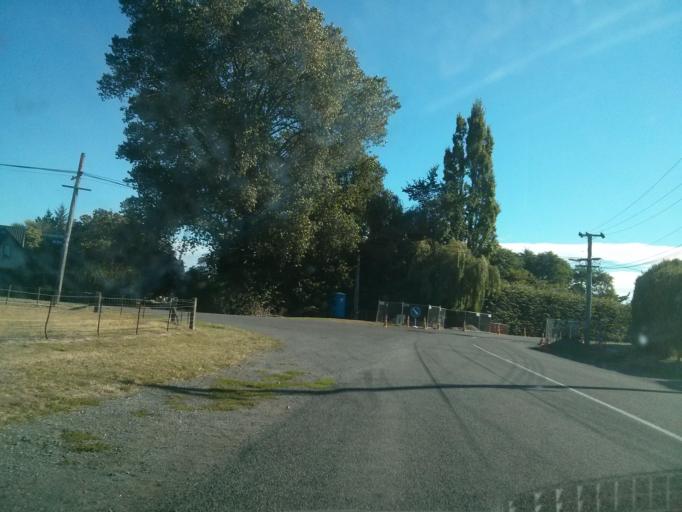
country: NZ
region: Canterbury
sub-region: Christchurch City
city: Christchurch
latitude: -43.4786
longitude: 172.5591
